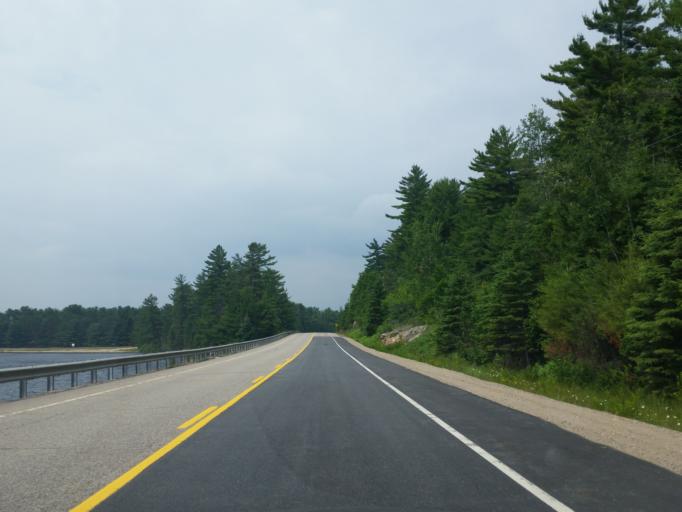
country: CA
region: Ontario
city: Mattawa
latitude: 45.5826
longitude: -78.4943
